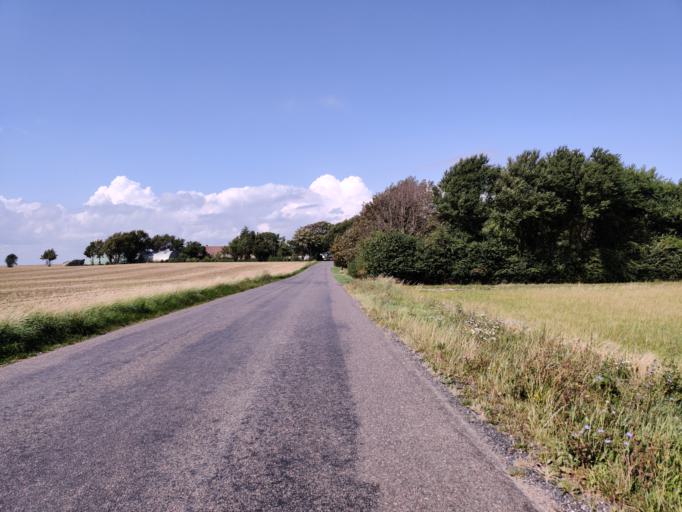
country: DK
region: Zealand
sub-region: Guldborgsund Kommune
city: Nykobing Falster
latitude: 54.6221
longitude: 11.9118
